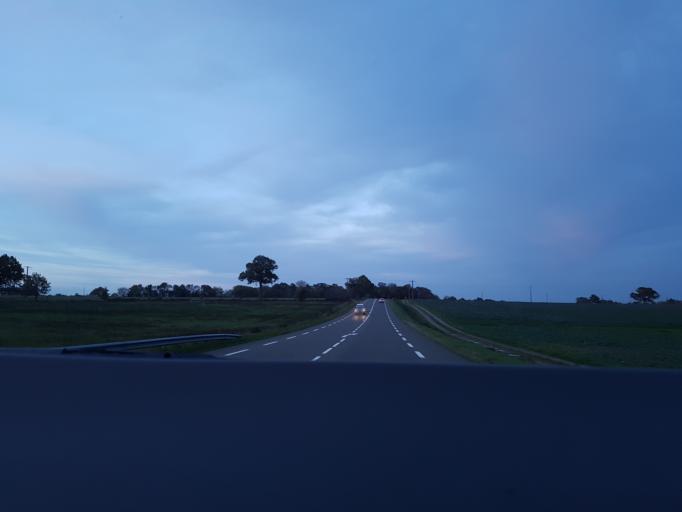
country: FR
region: Pays de la Loire
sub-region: Departement de la Mayenne
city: Ahuille
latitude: 47.9951
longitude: -0.8491
